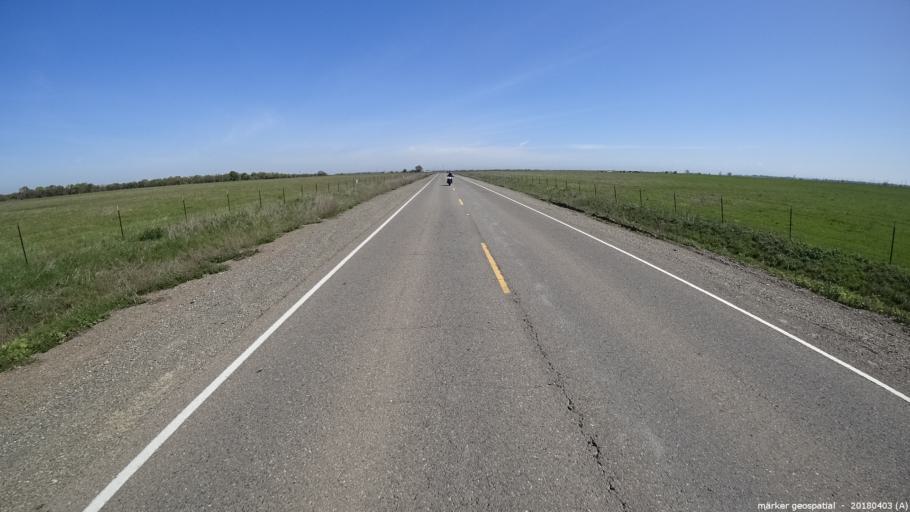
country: US
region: California
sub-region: Sacramento County
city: Wilton
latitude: 38.3601
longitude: -121.3132
